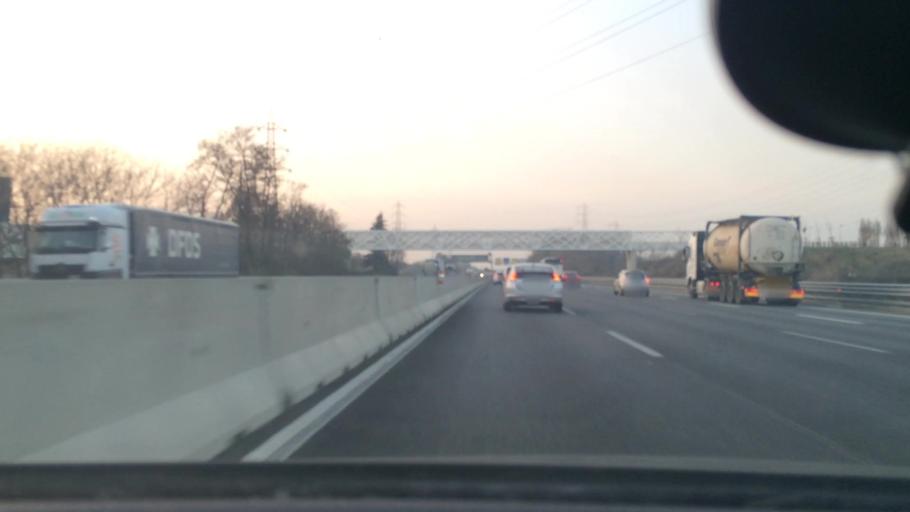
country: IT
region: Lombardy
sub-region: Citta metropolitana di Milano
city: Arese
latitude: 45.5382
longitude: 9.0789
